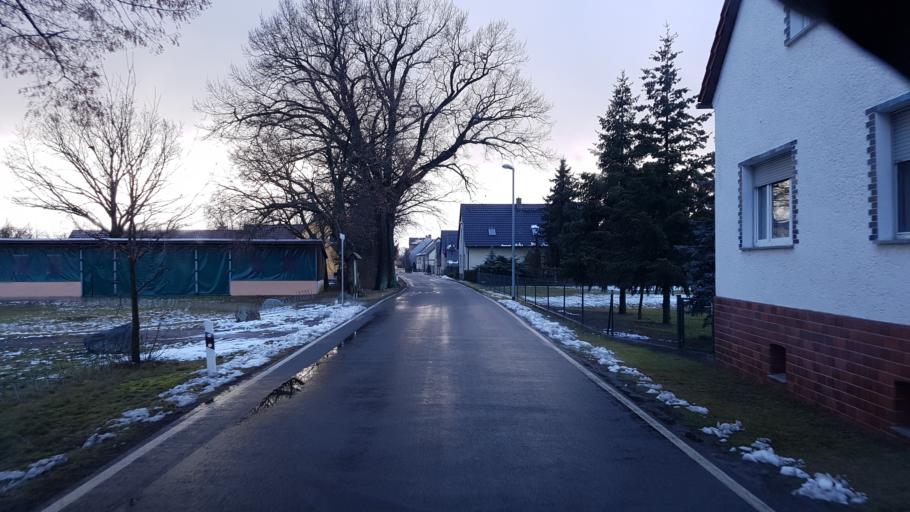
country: DE
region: Brandenburg
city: Heinersbruck
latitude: 51.8366
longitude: 14.5096
